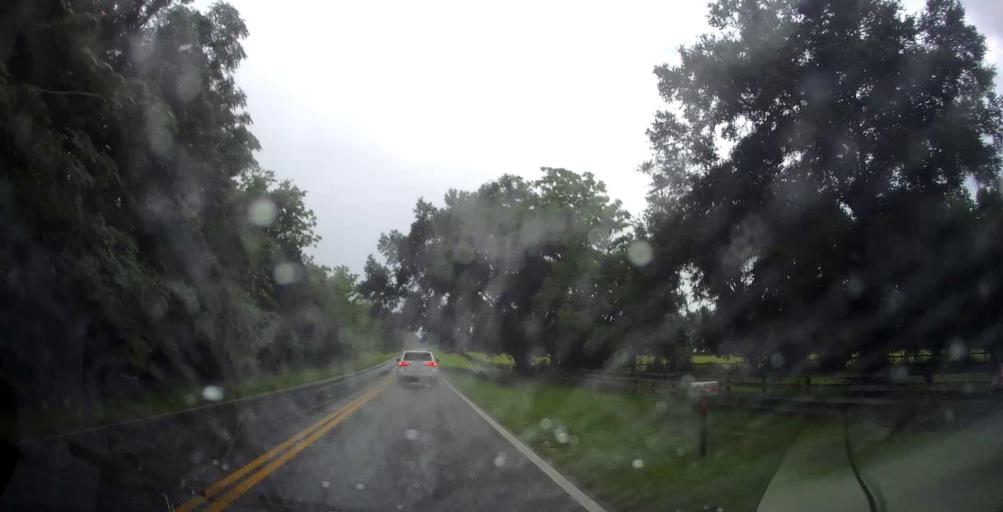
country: US
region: Florida
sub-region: Marion County
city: Ocala
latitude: 29.2490
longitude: -82.0896
